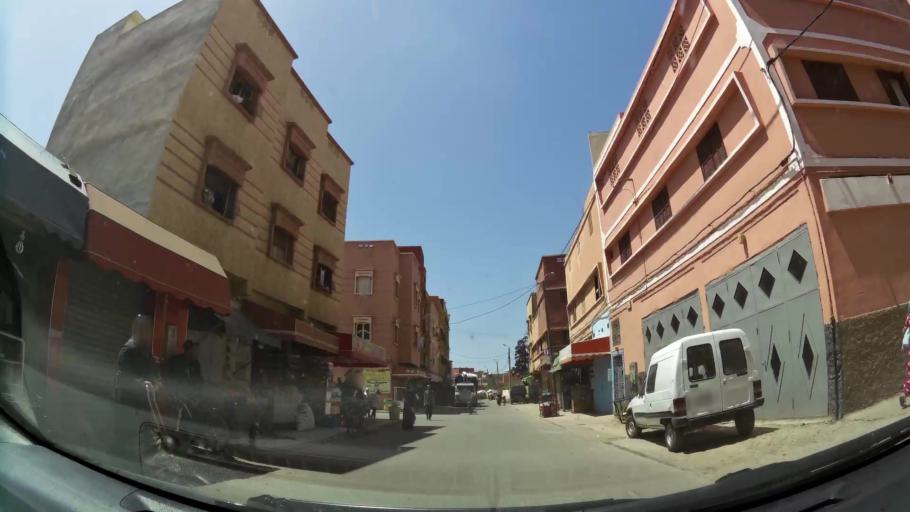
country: MA
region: Souss-Massa-Draa
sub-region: Inezgane-Ait Mellou
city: Inezgane
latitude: 30.3428
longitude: -9.4945
